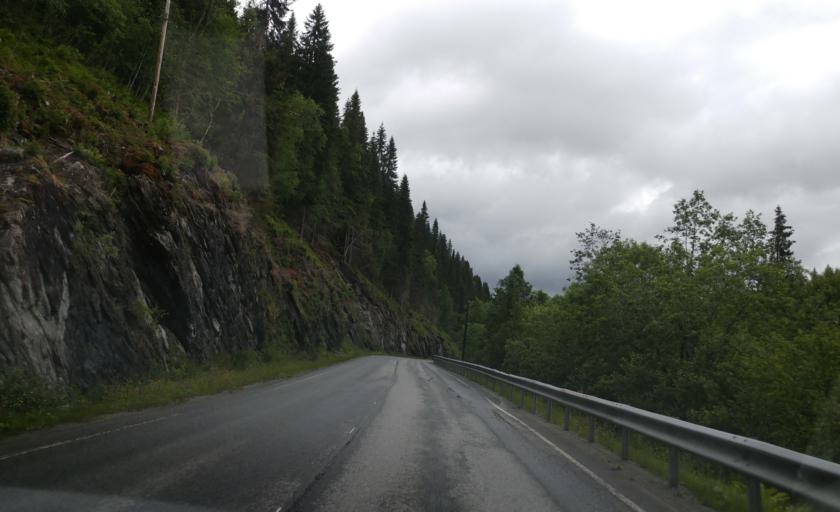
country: NO
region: Sor-Trondelag
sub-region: Selbu
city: Mebonden
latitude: 63.3100
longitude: 11.0802
